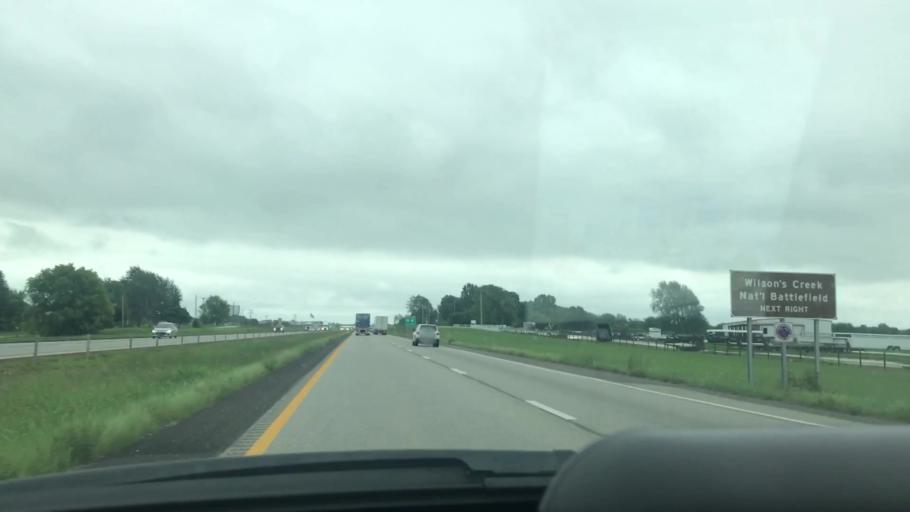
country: US
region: Missouri
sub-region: Greene County
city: Republic
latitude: 37.1977
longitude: -93.4364
